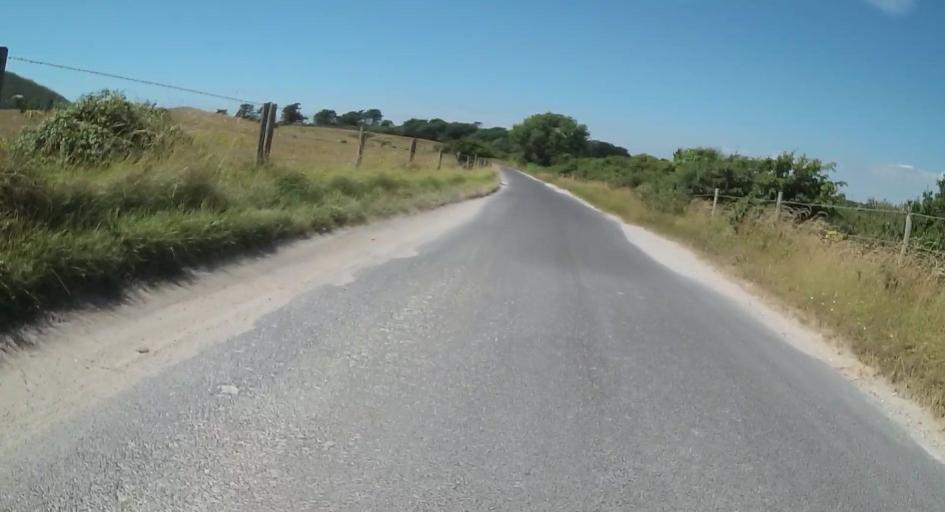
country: GB
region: England
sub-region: Dorset
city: Wool
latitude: 50.6304
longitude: -2.1818
